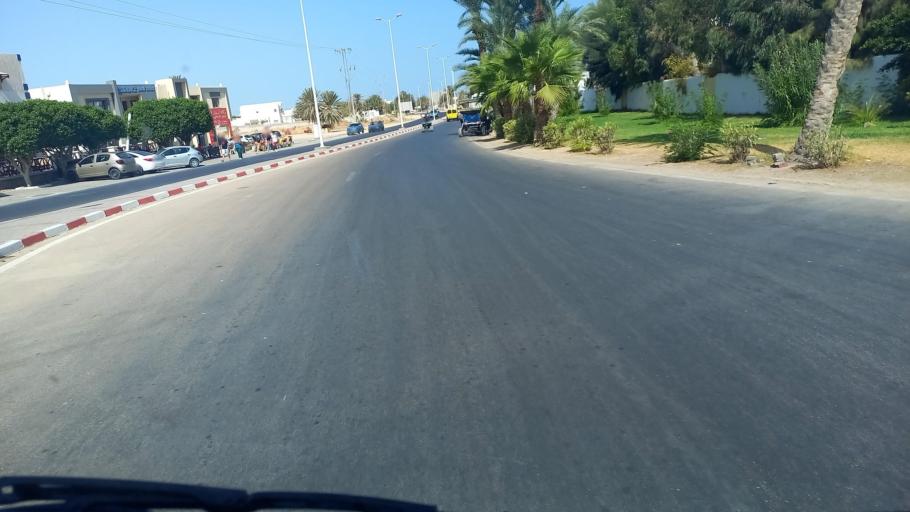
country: TN
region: Madanin
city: Midoun
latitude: 33.8245
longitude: 11.0412
